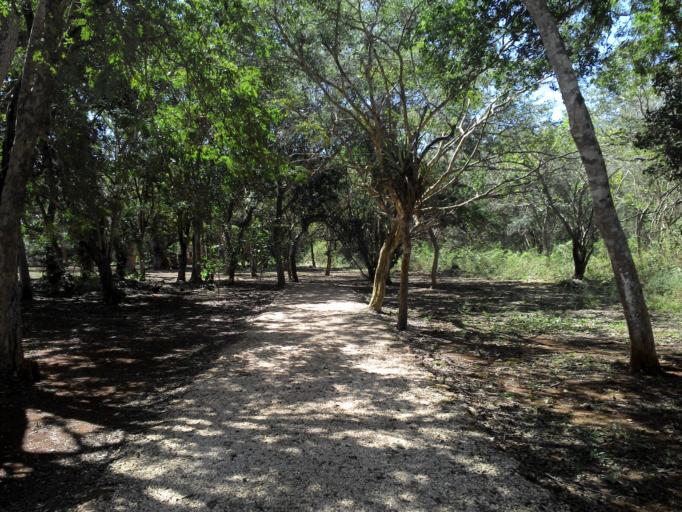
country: MX
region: Yucatan
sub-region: Oxkutzcab
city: Xul
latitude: 20.1735
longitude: -89.5794
